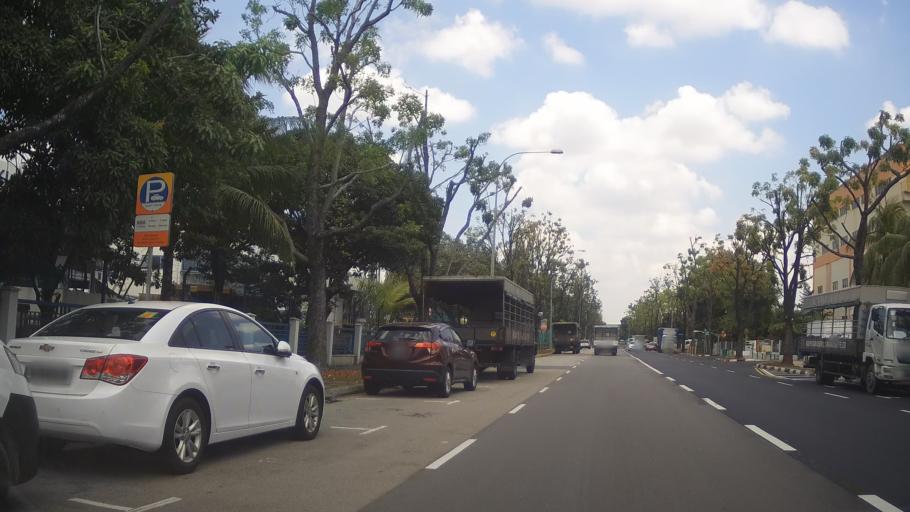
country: MY
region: Johor
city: Johor Bahru
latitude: 1.3056
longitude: 103.6562
